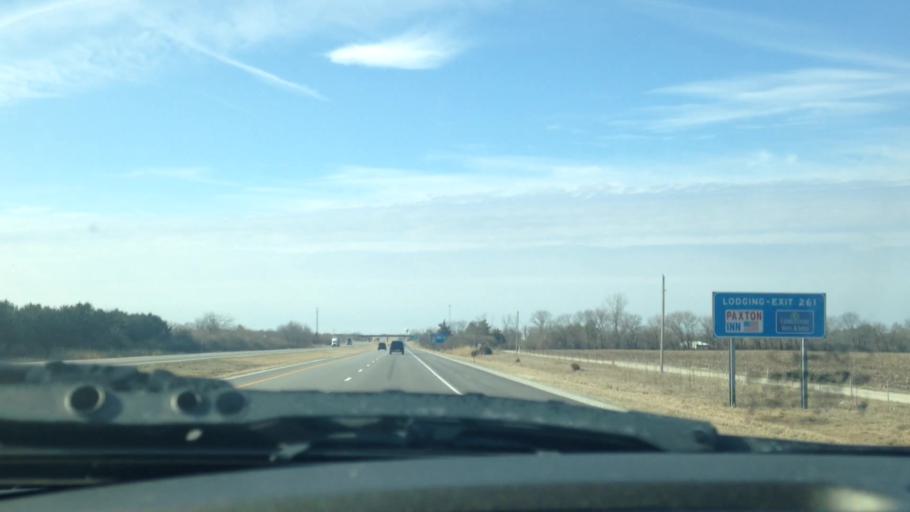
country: US
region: Illinois
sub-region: Ford County
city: Paxton
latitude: 40.4831
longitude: -88.0990
